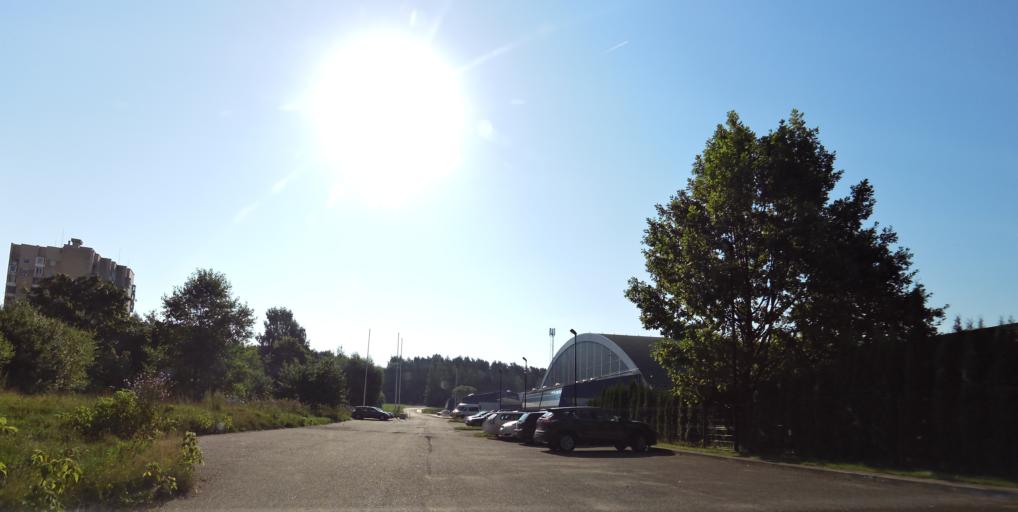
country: LT
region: Vilnius County
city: Seskine
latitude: 54.7093
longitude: 25.2346
